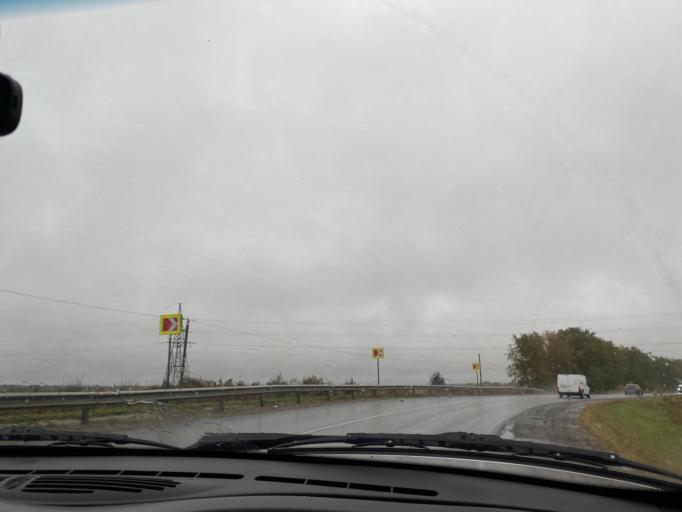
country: RU
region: Rjazan
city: Ryazan'
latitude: 54.4891
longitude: 39.8118
